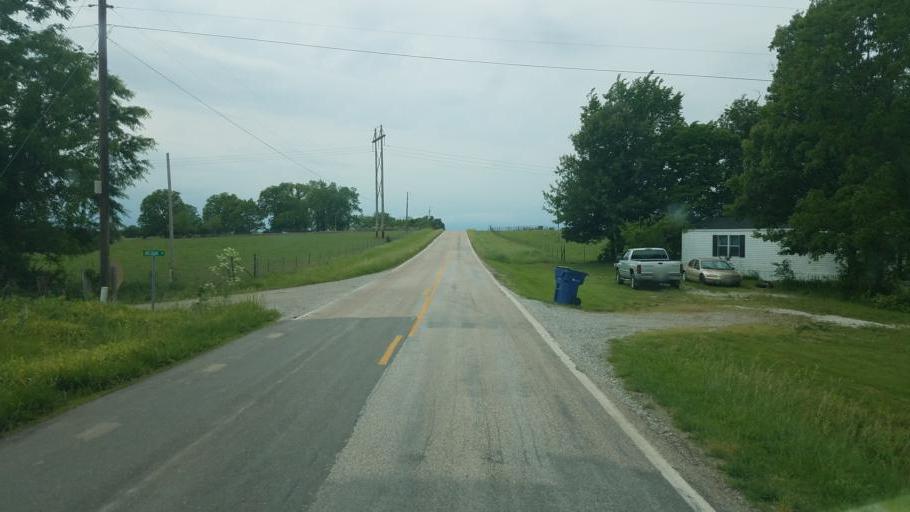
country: US
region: Missouri
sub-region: Moniteau County
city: California
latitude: 38.6840
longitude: -92.5978
